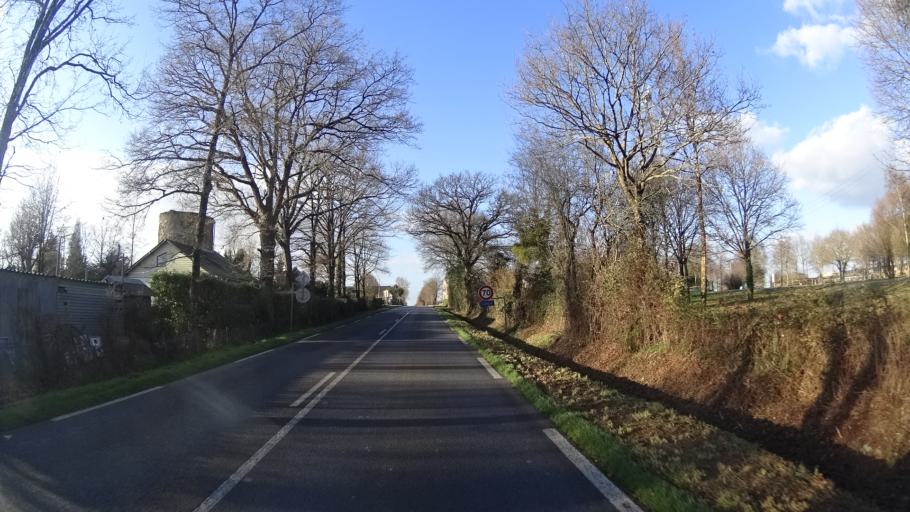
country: FR
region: Pays de la Loire
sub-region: Departement de la Loire-Atlantique
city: Guenrouet
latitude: 47.5368
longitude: -1.9257
